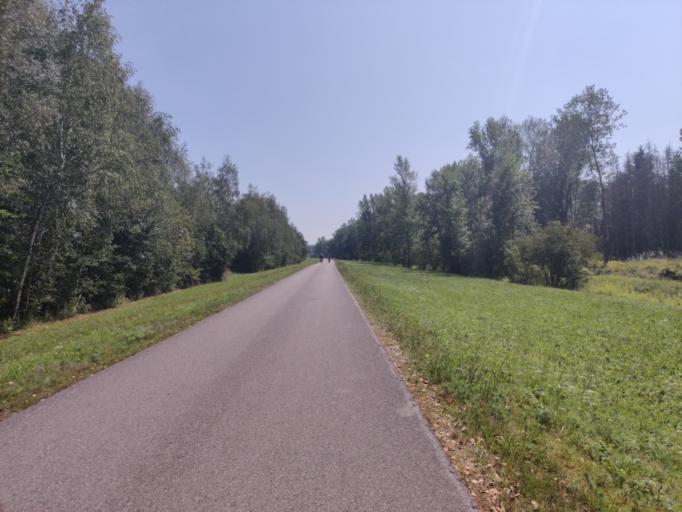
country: AT
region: Upper Austria
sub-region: Politischer Bezirk Urfahr-Umgebung
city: Feldkirchen an der Donau
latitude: 48.3262
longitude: 14.0417
